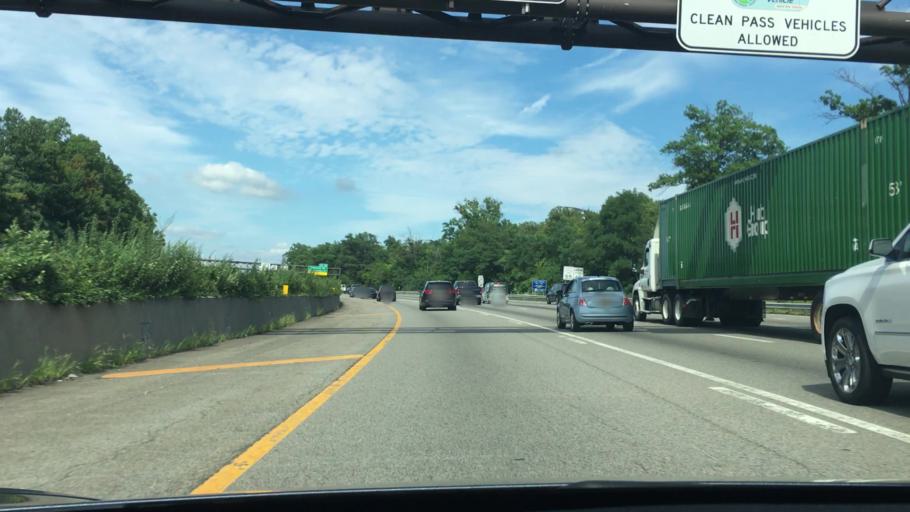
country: US
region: New York
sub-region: Nassau County
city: Lake Success
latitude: 40.7655
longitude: -73.7204
